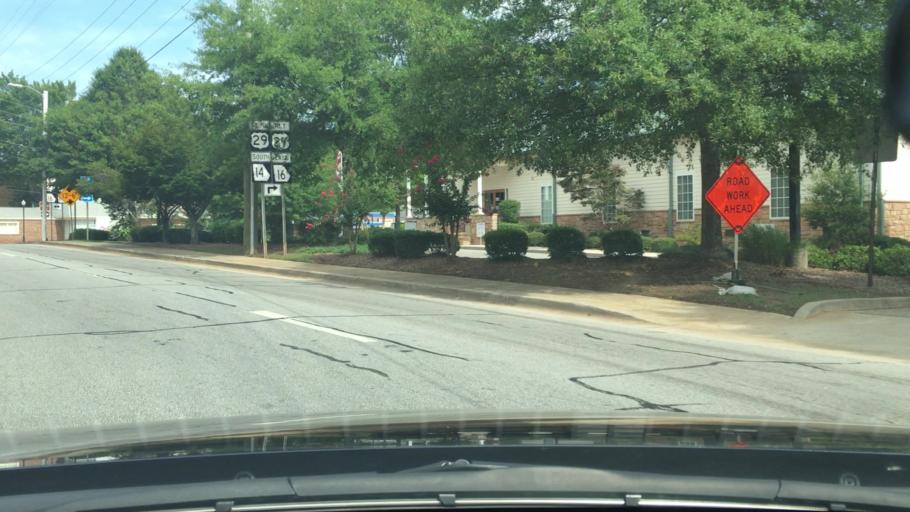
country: US
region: Georgia
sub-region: Coweta County
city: Newnan
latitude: 33.3722
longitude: -84.8006
